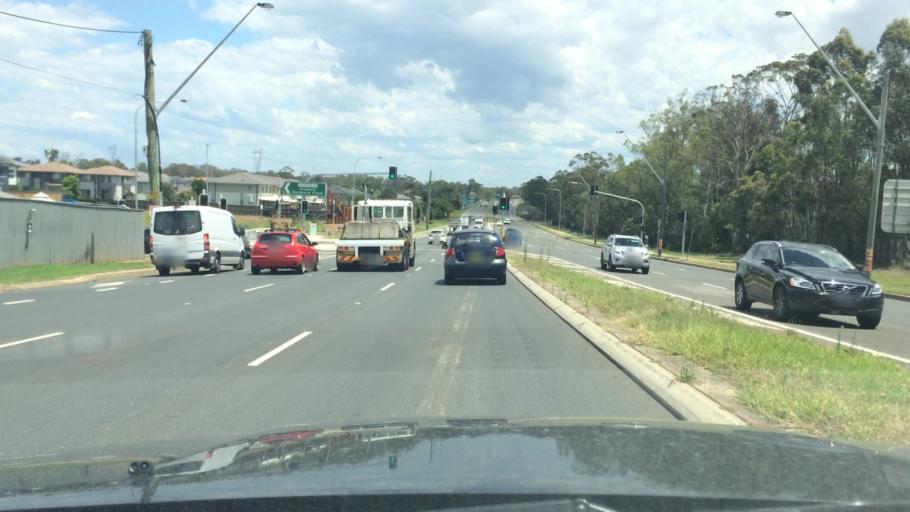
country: AU
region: New South Wales
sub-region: Campbelltown Municipality
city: Glenfield
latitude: -33.9590
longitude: 150.8860
